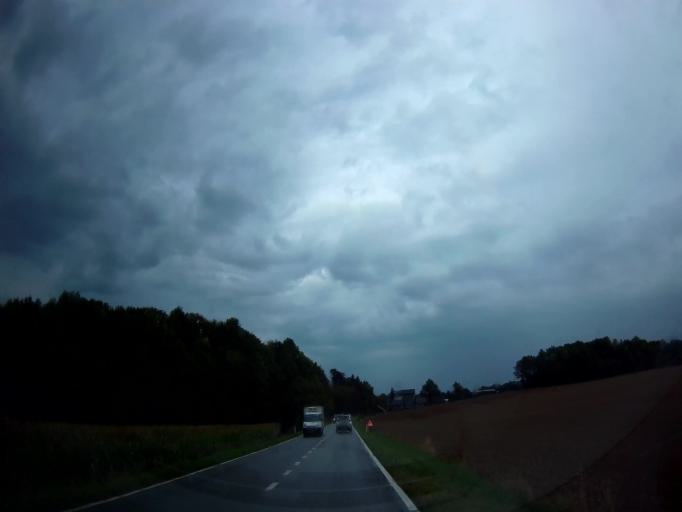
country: BE
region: Wallonia
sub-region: Province de Liege
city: Ferrieres
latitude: 50.4503
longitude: 5.6268
